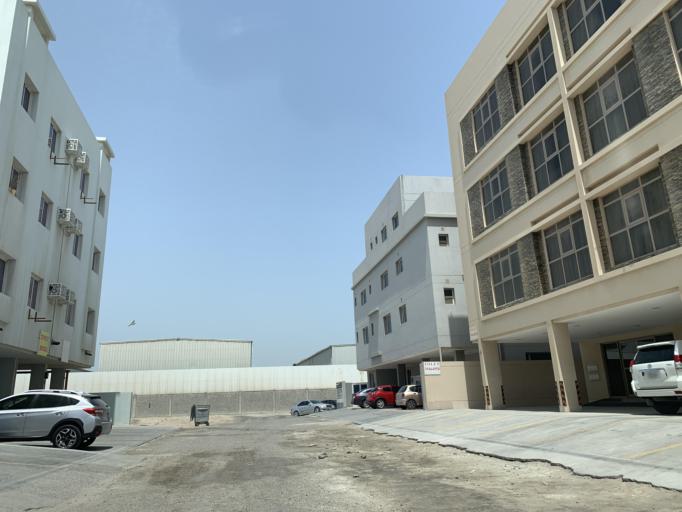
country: BH
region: Northern
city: Madinat `Isa
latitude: 26.1916
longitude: 50.5462
